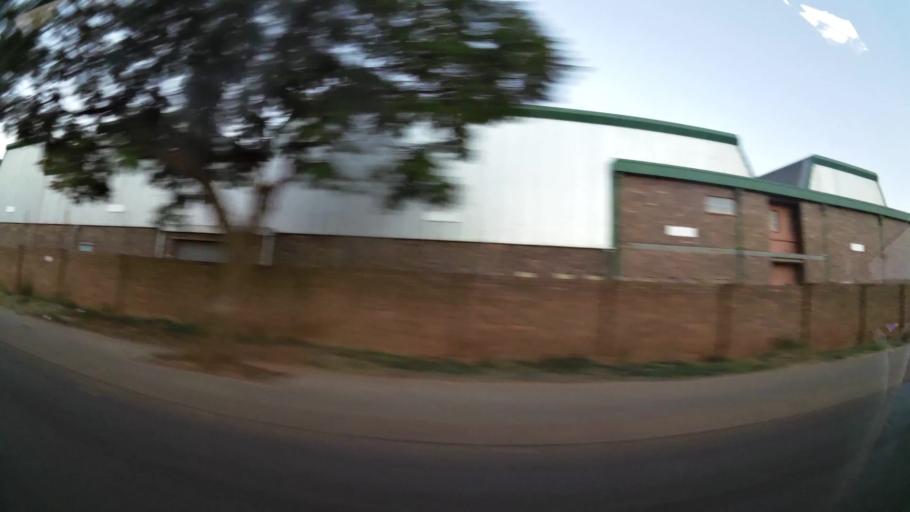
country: ZA
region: Gauteng
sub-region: City of Tshwane Metropolitan Municipality
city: Pretoria
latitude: -25.7279
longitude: 28.3221
